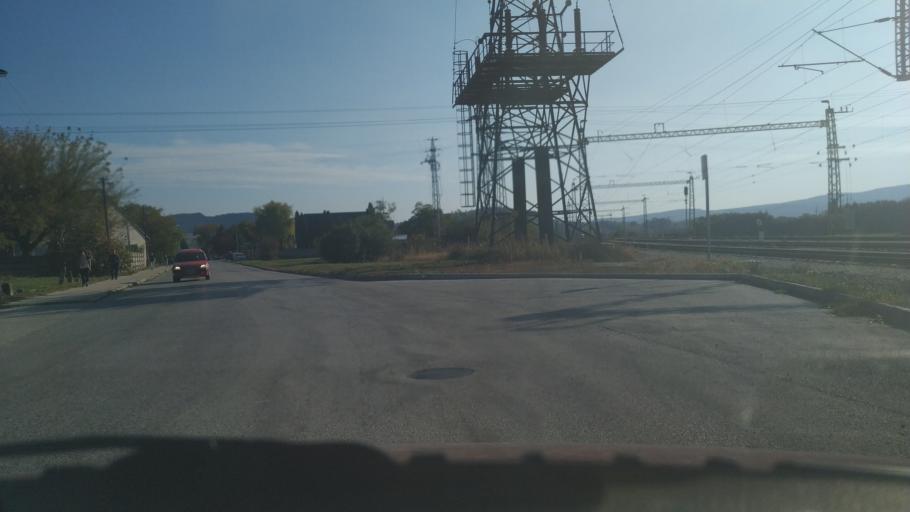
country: HU
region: Komarom-Esztergom
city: Esztergom
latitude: 47.7740
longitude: 18.7440
